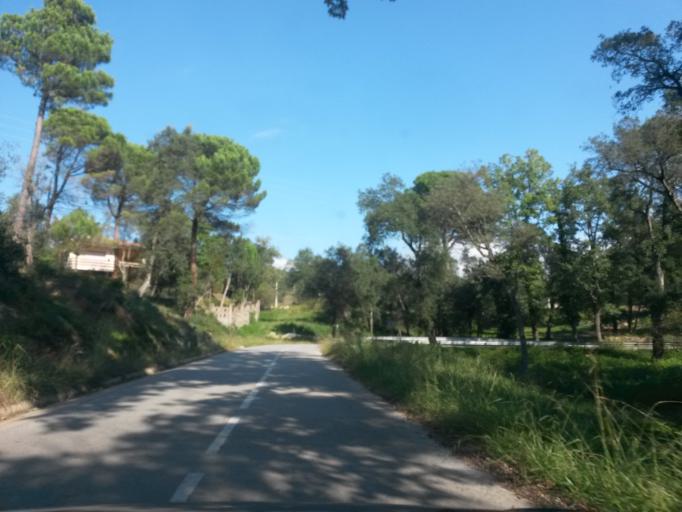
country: ES
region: Catalonia
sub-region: Provincia de Girona
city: Angles
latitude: 41.9521
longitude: 2.6876
